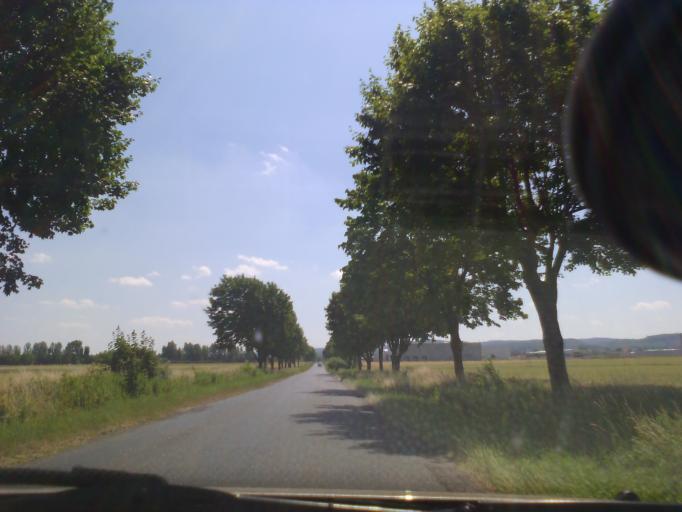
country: PL
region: Lower Silesian Voivodeship
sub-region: Powiat swidnicki
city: Swiebodzice
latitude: 50.8820
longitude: 16.3268
